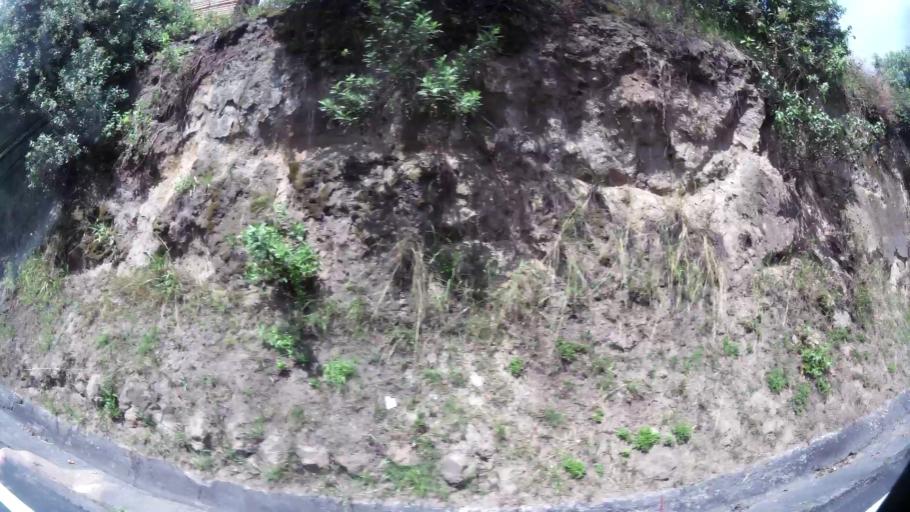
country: EC
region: Pichincha
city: Quito
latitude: -0.2019
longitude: -78.3742
